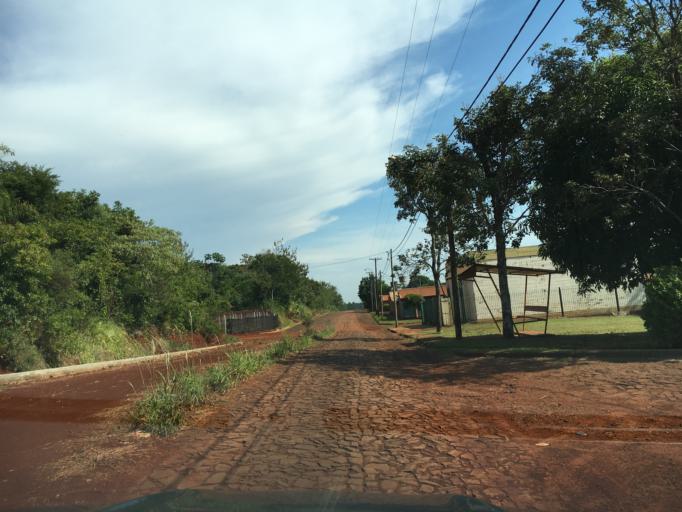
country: AR
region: Misiones
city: Puerto Rico
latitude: -26.8047
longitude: -55.0034
